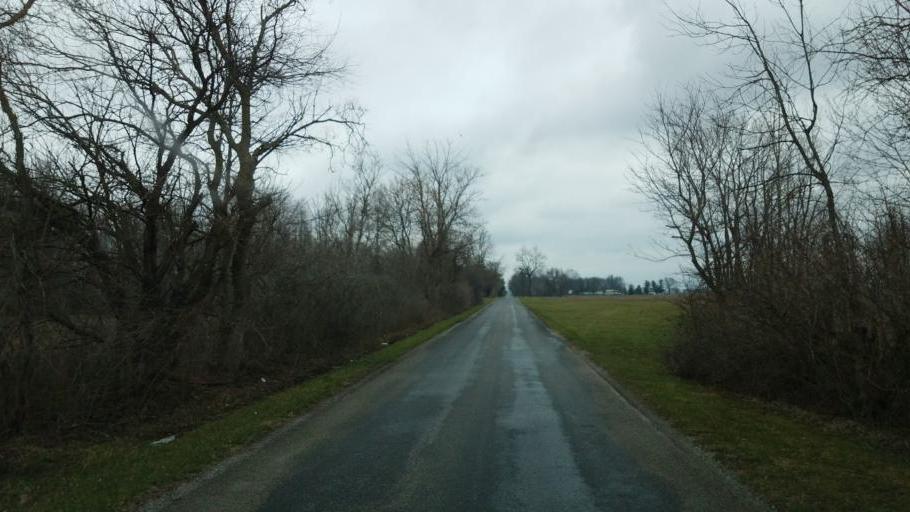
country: US
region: Ohio
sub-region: Delaware County
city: Ashley
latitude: 40.3633
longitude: -82.9872
